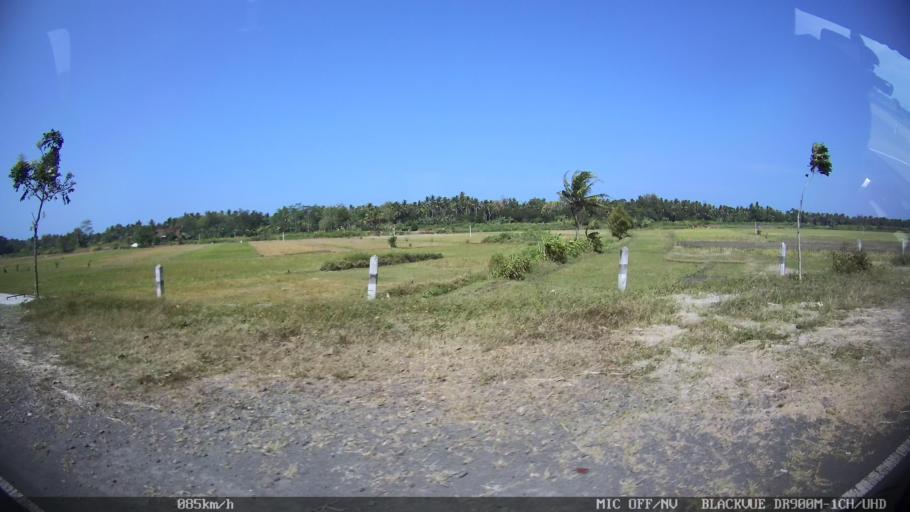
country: ID
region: Daerah Istimewa Yogyakarta
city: Srandakan
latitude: -7.9544
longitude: 110.1954
